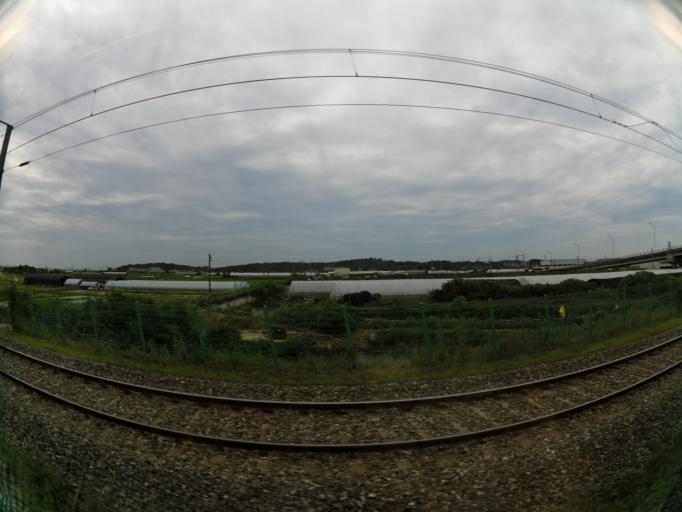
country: KR
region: Gyeonggi-do
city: Osan
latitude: 37.1130
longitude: 127.0627
